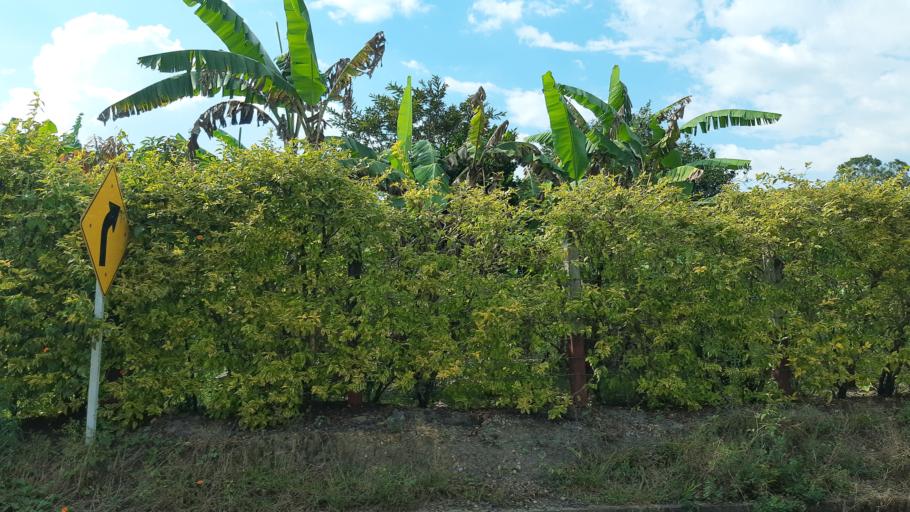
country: CO
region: Boyaca
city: Moniquira
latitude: 5.8437
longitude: -73.5814
